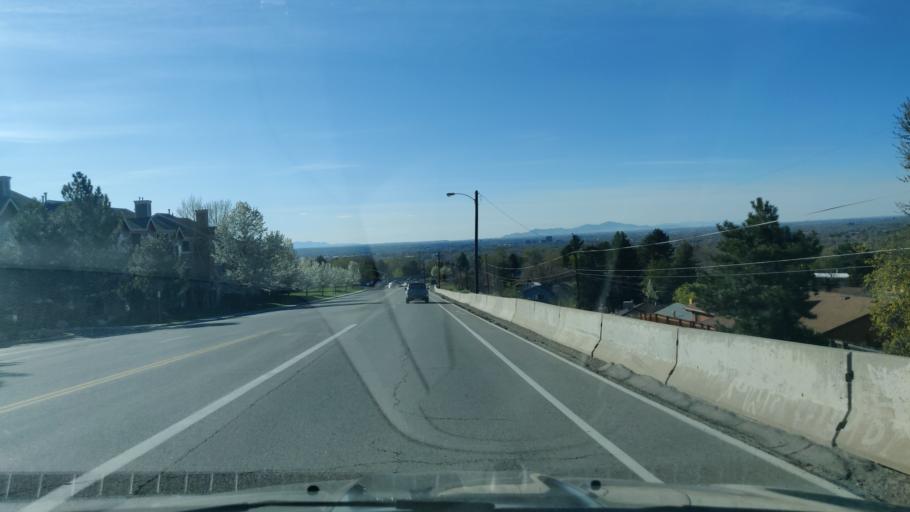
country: US
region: Utah
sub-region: Salt Lake County
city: Little Cottonwood Creek Valley
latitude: 40.6141
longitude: -111.8306
